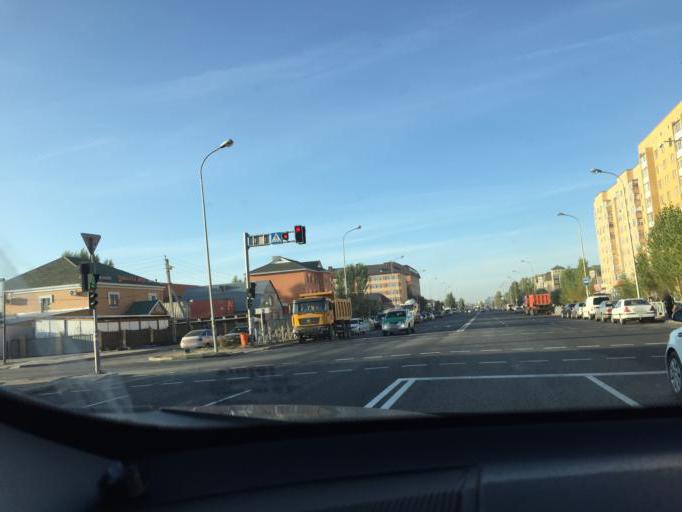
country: KZ
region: Astana Qalasy
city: Astana
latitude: 51.1554
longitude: 71.5112
